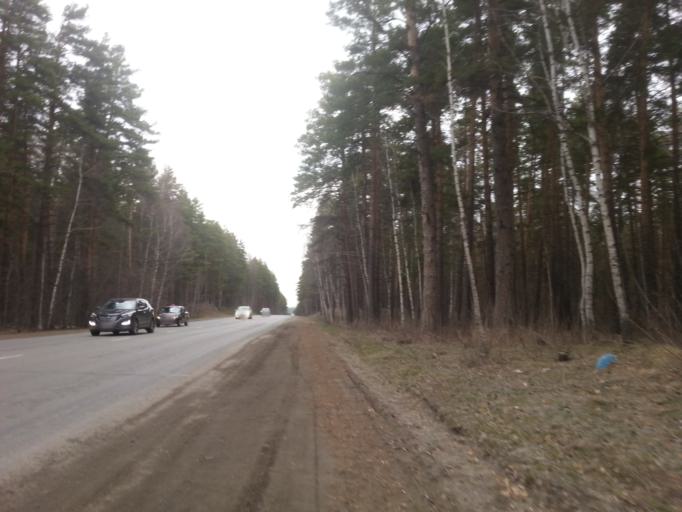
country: RU
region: Altai Krai
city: Yuzhnyy
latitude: 53.2802
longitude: 83.7172
